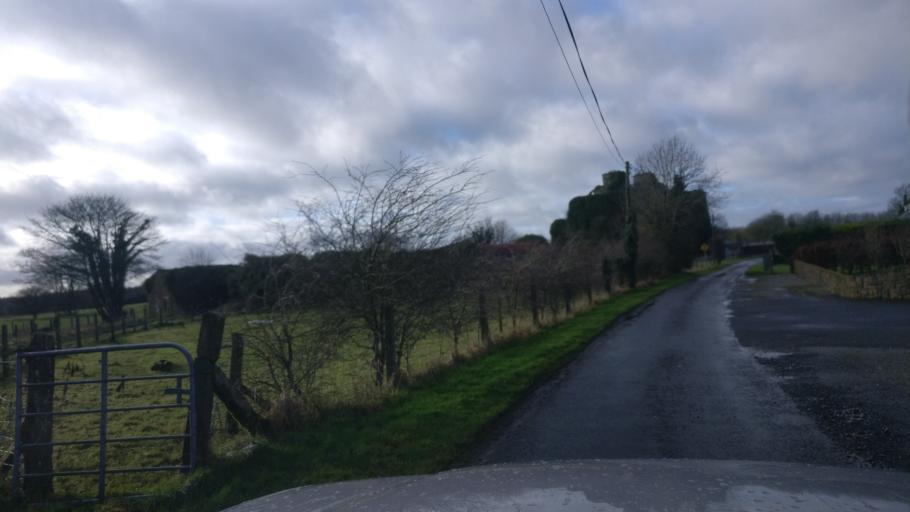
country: IE
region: Connaught
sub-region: County Galway
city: Loughrea
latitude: 53.2442
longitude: -8.6288
